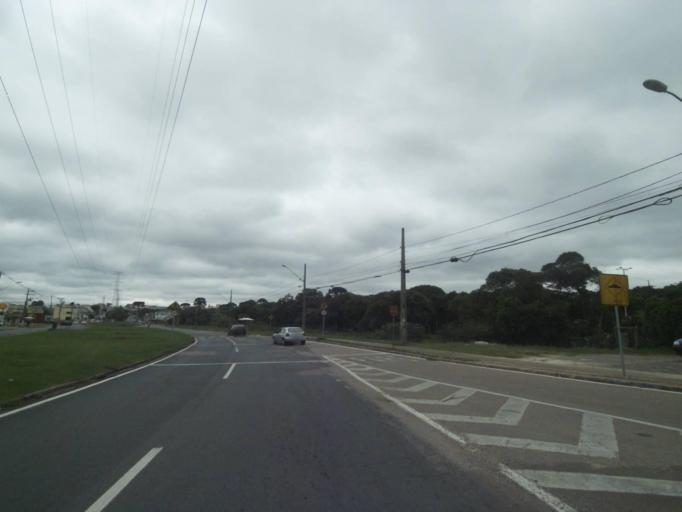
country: BR
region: Parana
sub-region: Araucaria
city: Araucaria
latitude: -25.5552
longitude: -49.3330
